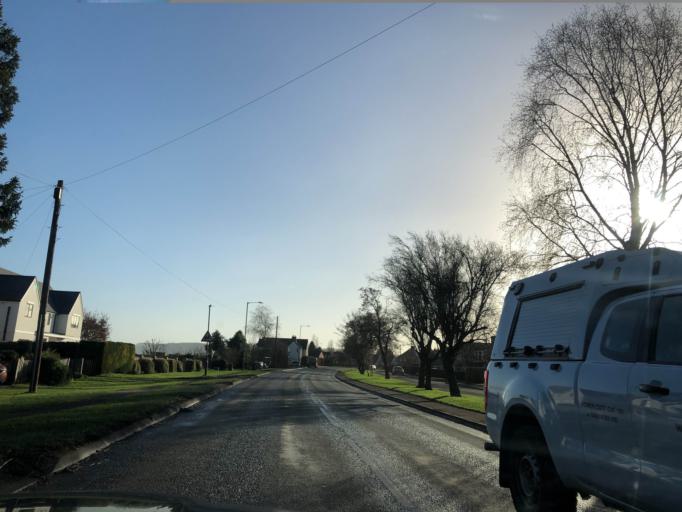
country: GB
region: England
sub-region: Warwickshire
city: Wellesbourne Mountford
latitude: 52.1949
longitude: -1.5888
